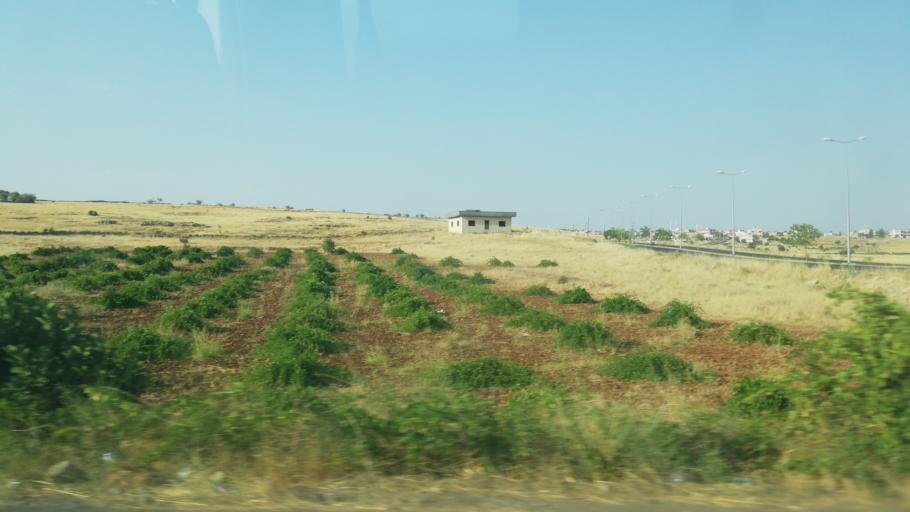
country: TR
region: Mardin
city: Acirli
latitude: 37.4456
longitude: 41.2824
